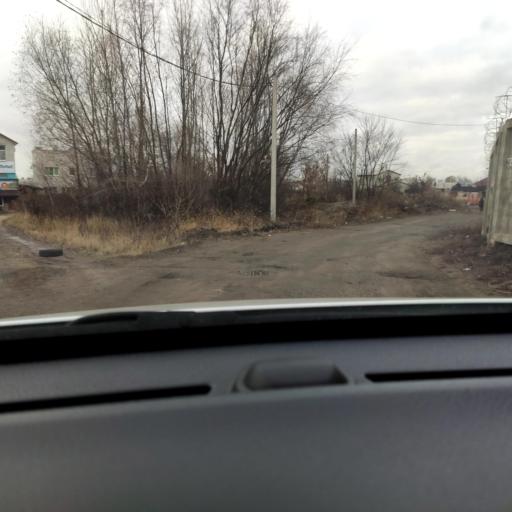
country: RU
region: Voronezj
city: Maslovka
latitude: 51.6104
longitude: 39.2166
